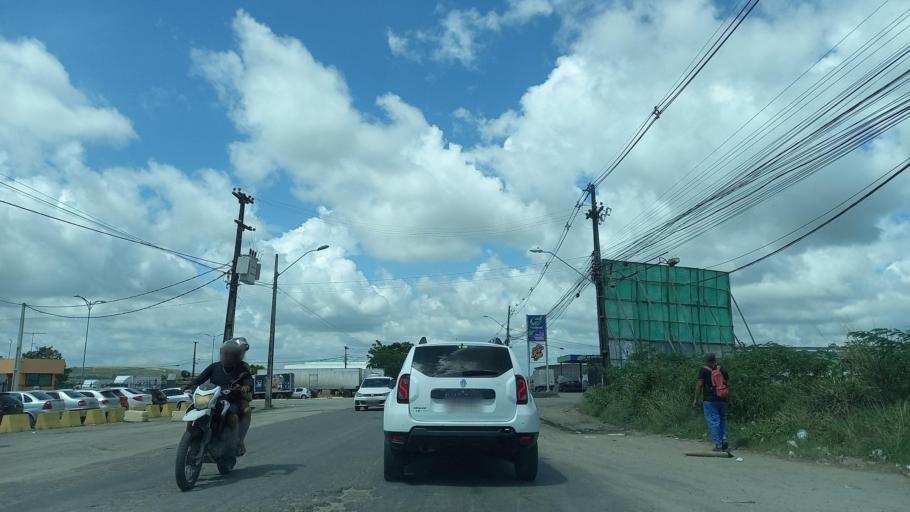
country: BR
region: Pernambuco
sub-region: Jaboatao Dos Guararapes
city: Jaboatao
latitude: -8.1549
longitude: -34.9620
